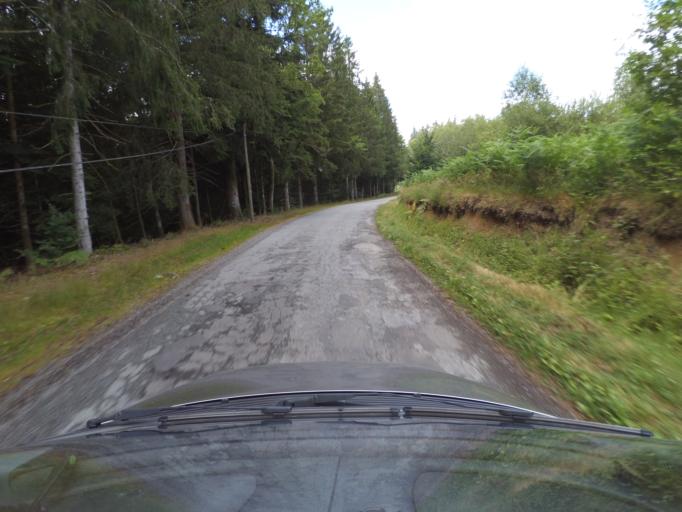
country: FR
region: Limousin
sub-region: Departement de la Creuse
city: Banize
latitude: 45.7649
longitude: 1.9484
